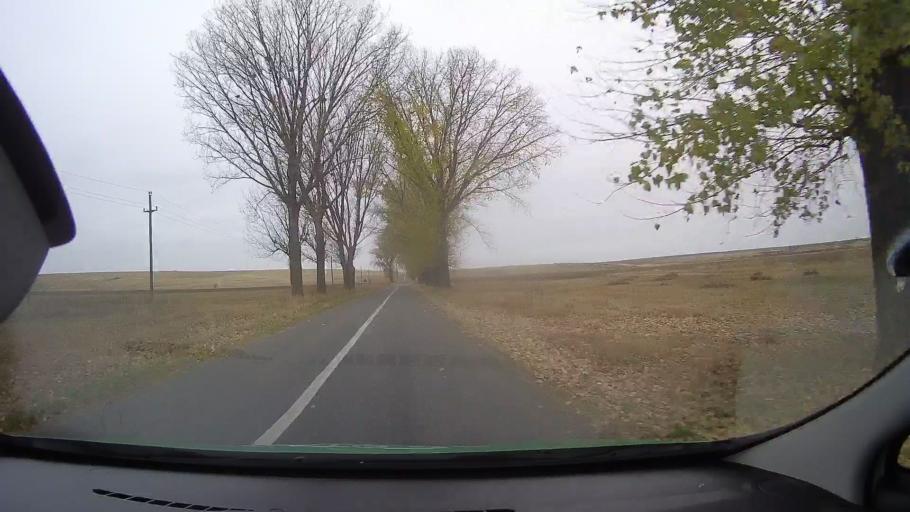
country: RO
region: Constanta
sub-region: Comuna Saraiu
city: Saraiu
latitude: 44.7268
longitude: 28.2200
